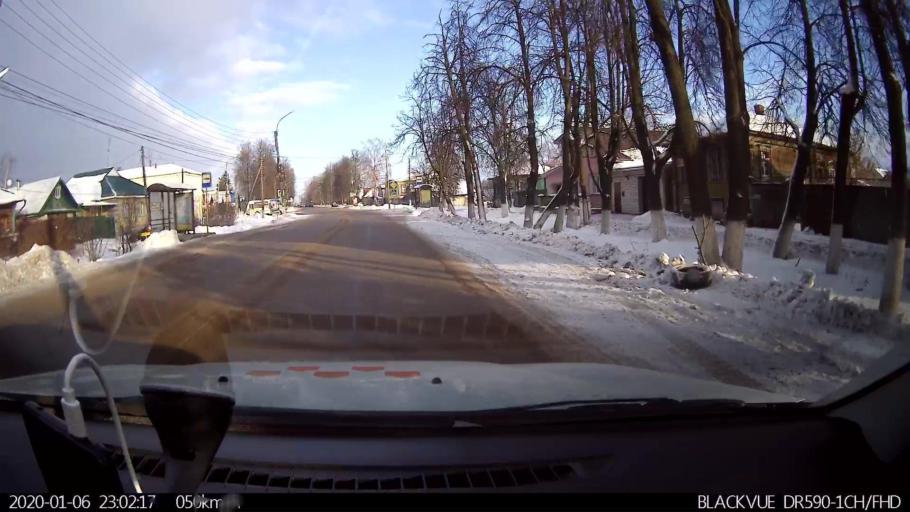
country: RU
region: Nizjnij Novgorod
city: Bogorodsk
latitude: 56.1088
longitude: 43.5277
